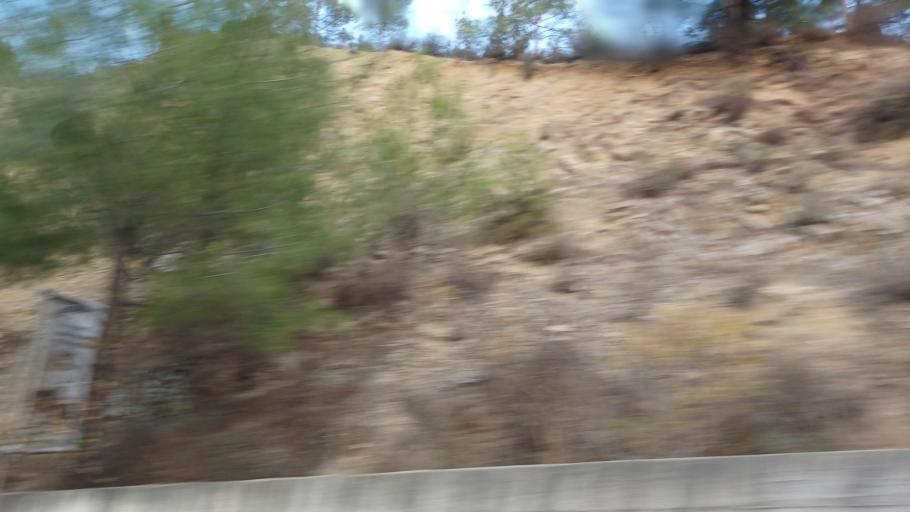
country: CY
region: Lefkosia
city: Kakopetria
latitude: 34.9721
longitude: 32.9196
